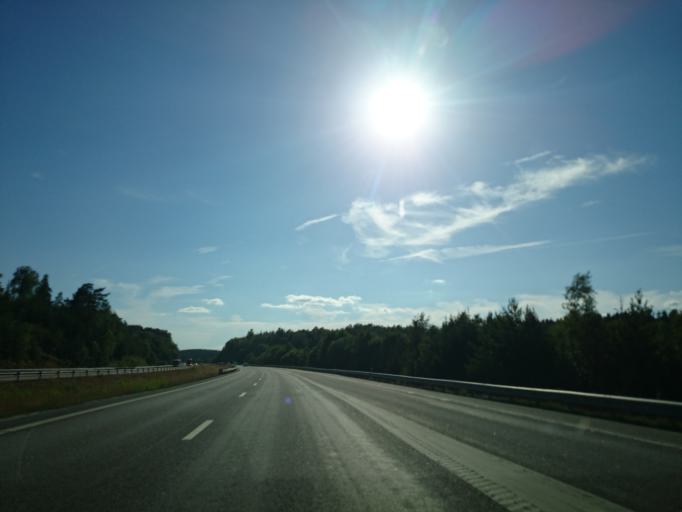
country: SE
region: Soedermanland
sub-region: Gnesta Kommun
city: Gnesta
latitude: 58.9087
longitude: 17.3320
